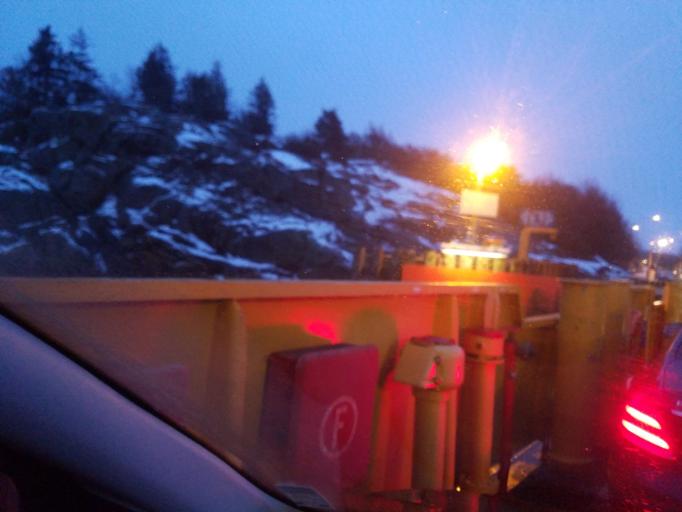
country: SE
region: Vaestra Goetaland
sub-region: Lysekils Kommun
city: Brastad
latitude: 58.3009
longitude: 11.5342
